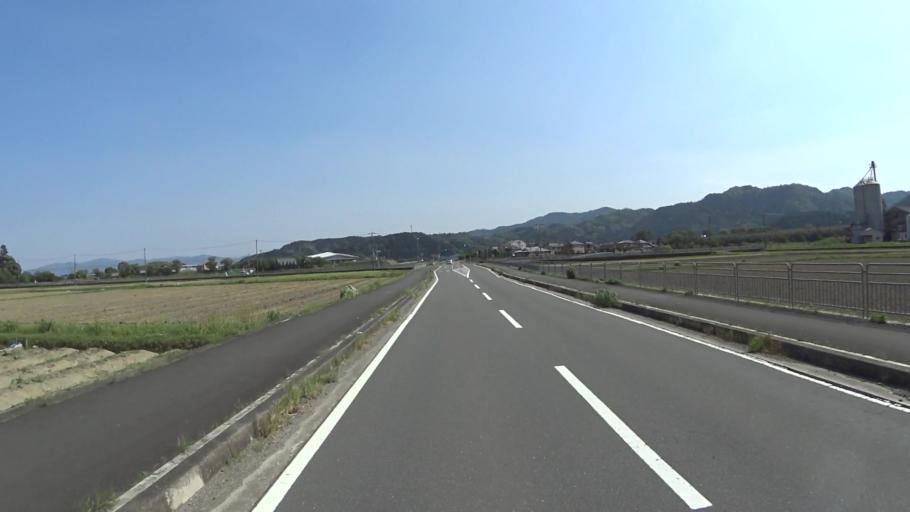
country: JP
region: Kyoto
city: Kameoka
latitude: 35.0792
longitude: 135.5371
